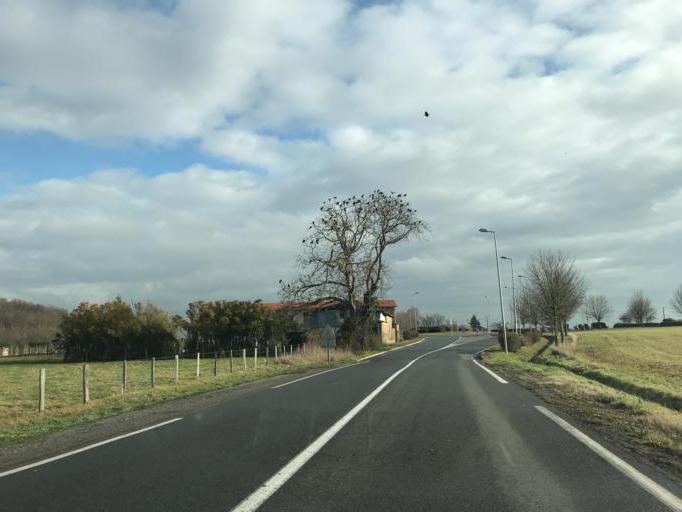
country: FR
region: Rhone-Alpes
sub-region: Departement de l'Ain
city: Civrieux
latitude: 45.9351
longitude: 4.8801
